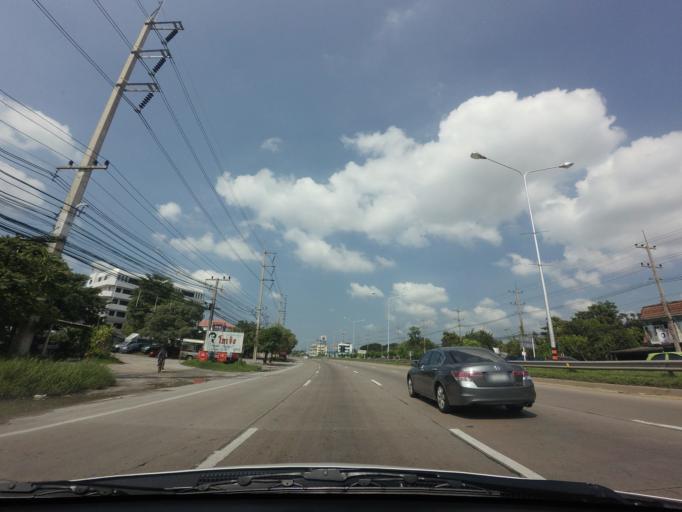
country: TH
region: Nakhon Pathom
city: Sam Phran
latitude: 13.7416
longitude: 100.2392
